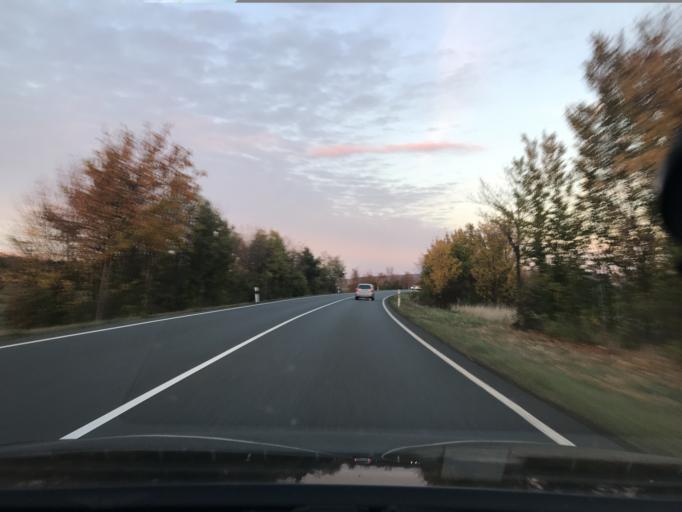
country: DE
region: Thuringia
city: Monchenholzhausen
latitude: 50.9697
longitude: 11.1679
